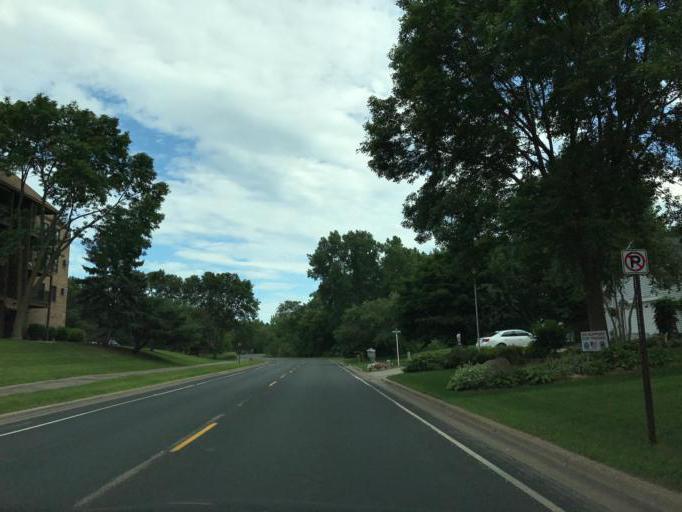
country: US
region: Minnesota
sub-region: Hennepin County
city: Osseo
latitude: 45.0812
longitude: -93.4060
